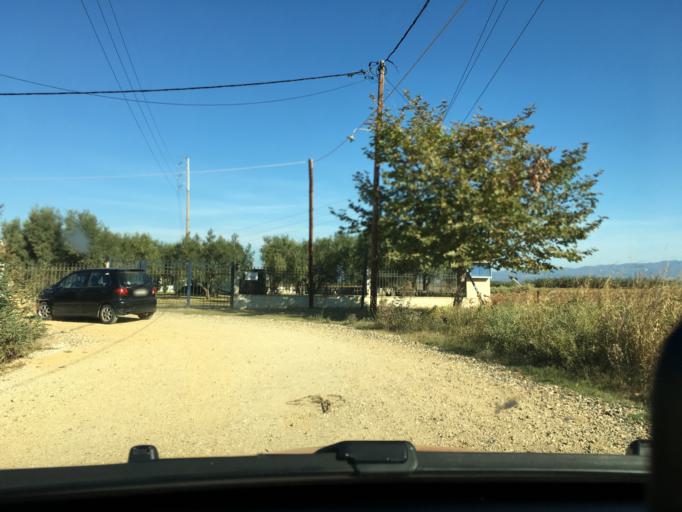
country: GR
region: Central Macedonia
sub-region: Nomos Chalkidikis
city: Nea Potidhaia
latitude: 40.2077
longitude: 23.3285
